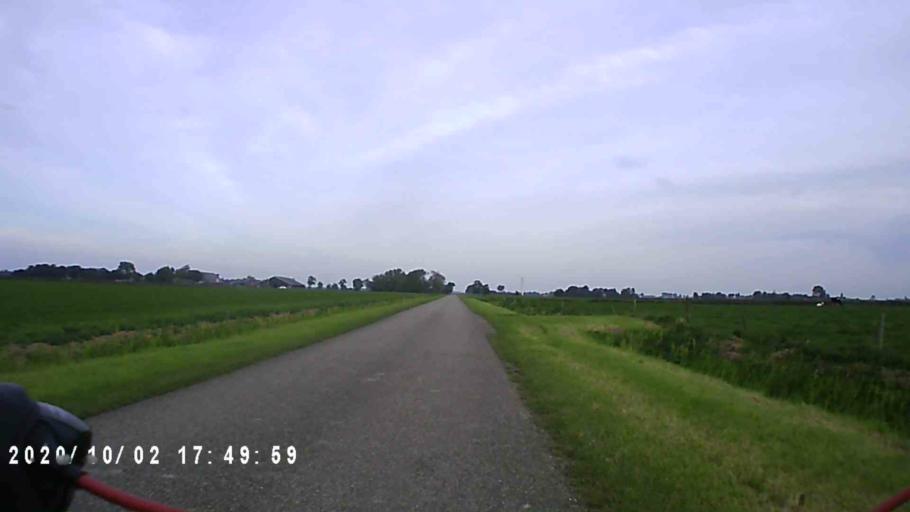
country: NL
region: Groningen
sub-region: Gemeente Zuidhorn
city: Oldehove
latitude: 53.3361
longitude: 6.4086
